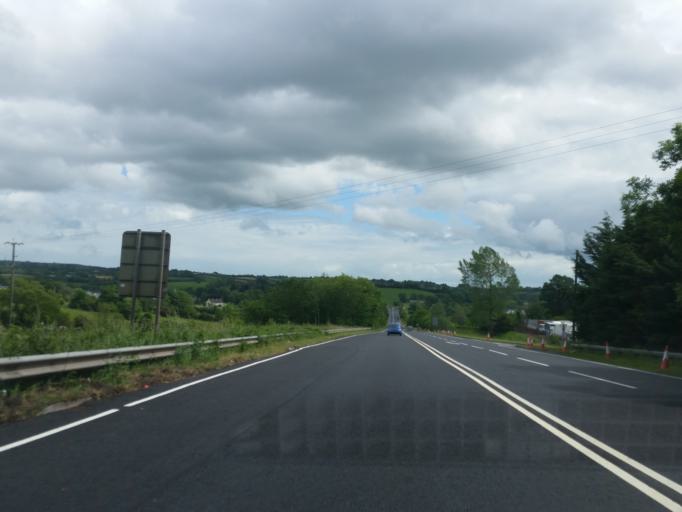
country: IE
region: Ulster
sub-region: County Monaghan
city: Monaghan
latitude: 54.4652
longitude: -7.0441
